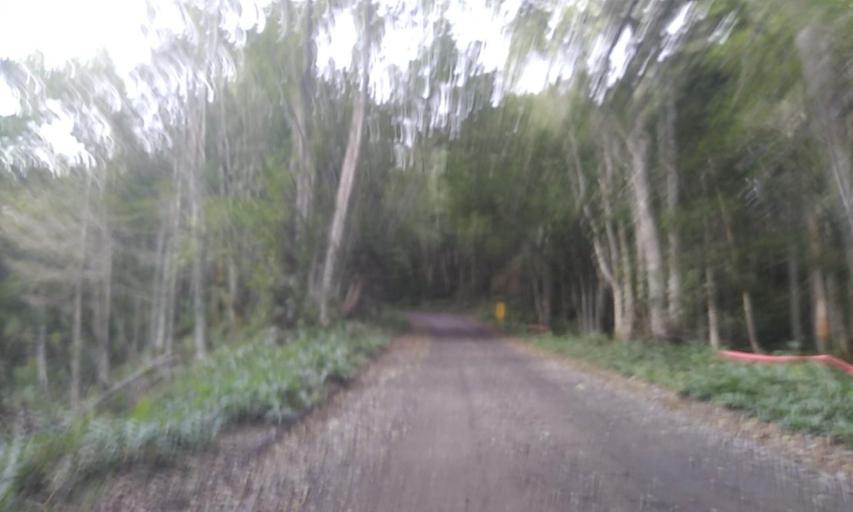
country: JP
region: Hokkaido
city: Abashiri
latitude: 43.6587
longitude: 144.5514
